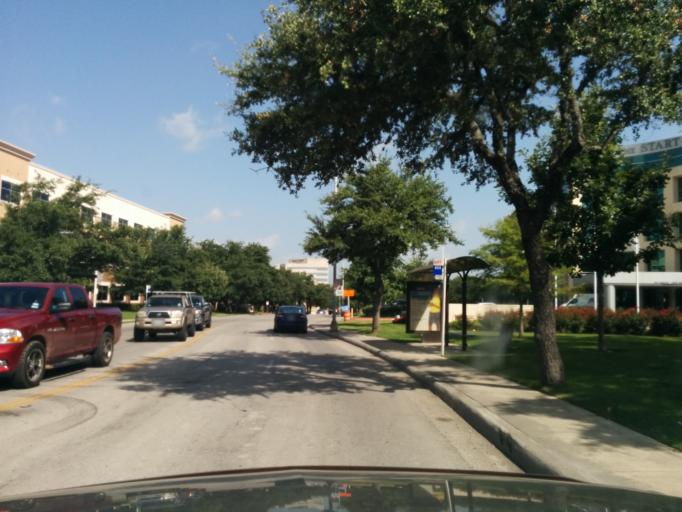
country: US
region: Texas
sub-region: Bexar County
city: Balcones Heights
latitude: 29.5107
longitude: -98.5716
